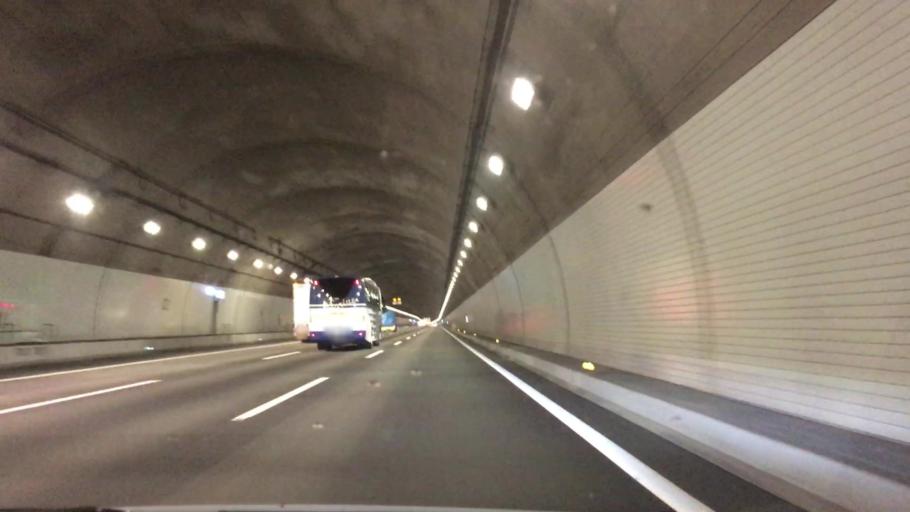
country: JP
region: Shizuoka
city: Fujieda
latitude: 34.9561
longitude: 138.2860
